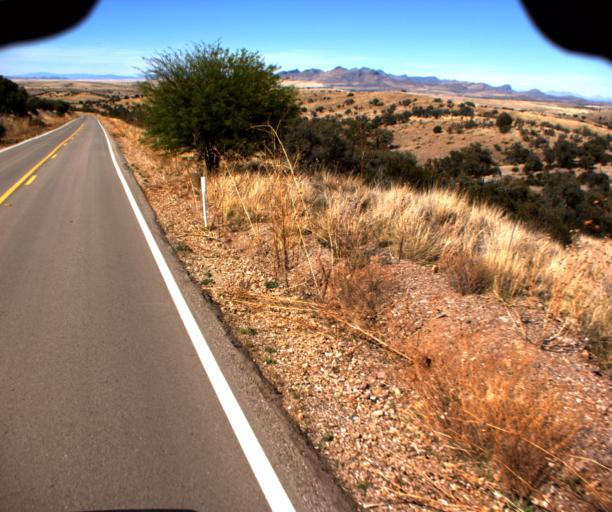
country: US
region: Arizona
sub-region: Cochise County
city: Huachuca City
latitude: 31.5388
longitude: -110.5046
